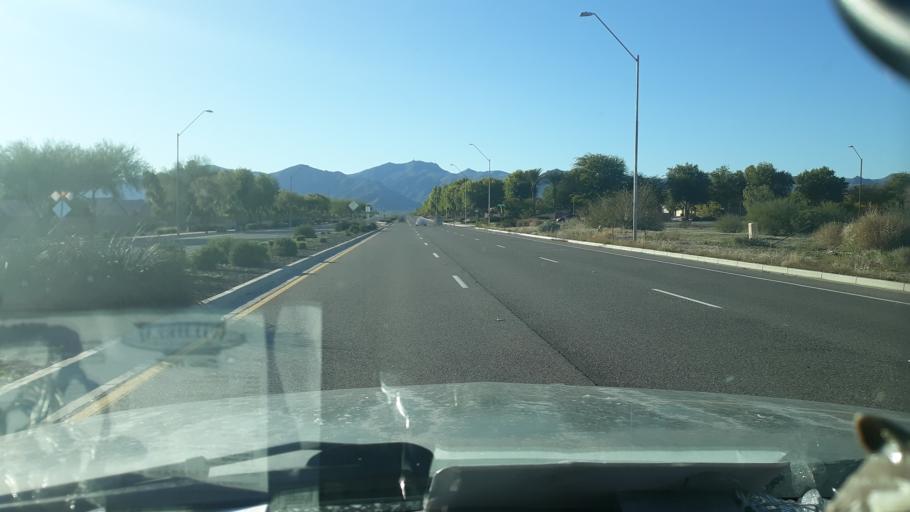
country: US
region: Arizona
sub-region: Maricopa County
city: Citrus Park
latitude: 33.5662
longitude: -112.4472
